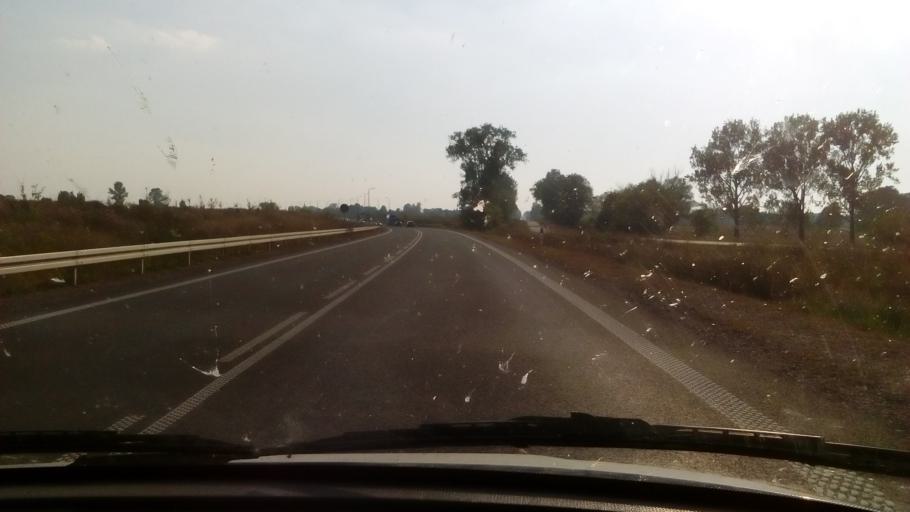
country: PL
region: Podlasie
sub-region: Powiat grajewski
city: Rajgrod
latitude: 53.7822
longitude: 22.8438
